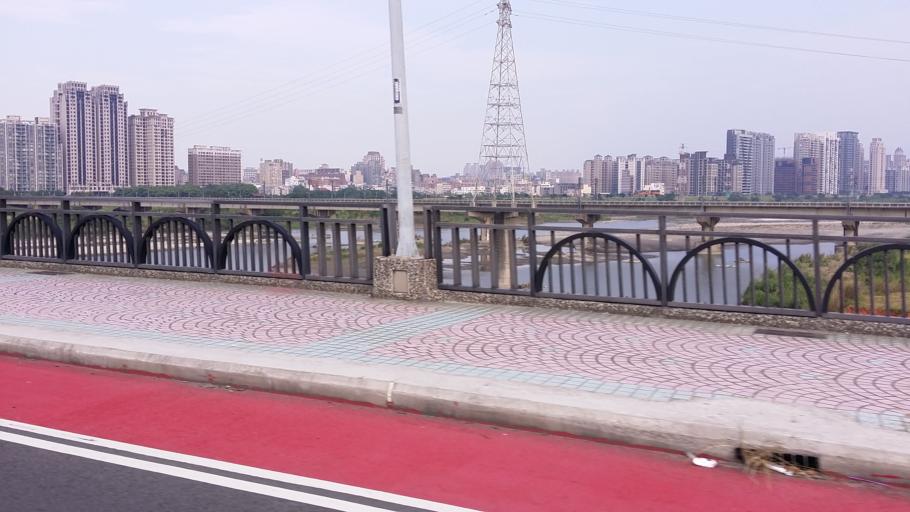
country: TW
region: Taiwan
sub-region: Hsinchu
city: Zhubei
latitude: 24.8216
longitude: 120.9965
